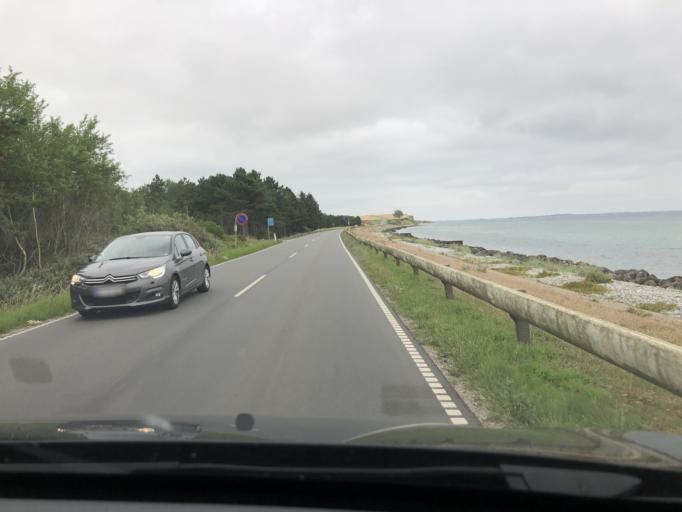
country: DK
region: South Denmark
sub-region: AEro Kommune
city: Marstal
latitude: 54.8405
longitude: 10.4631
